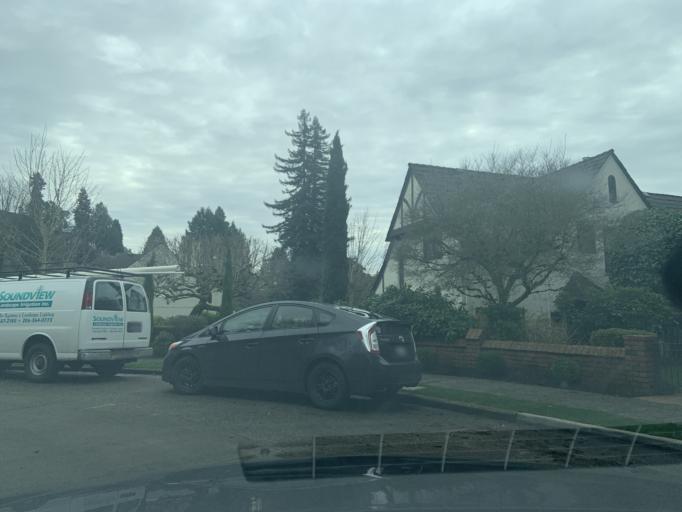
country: US
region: Washington
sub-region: King County
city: Medina
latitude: 47.6543
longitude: -122.2800
